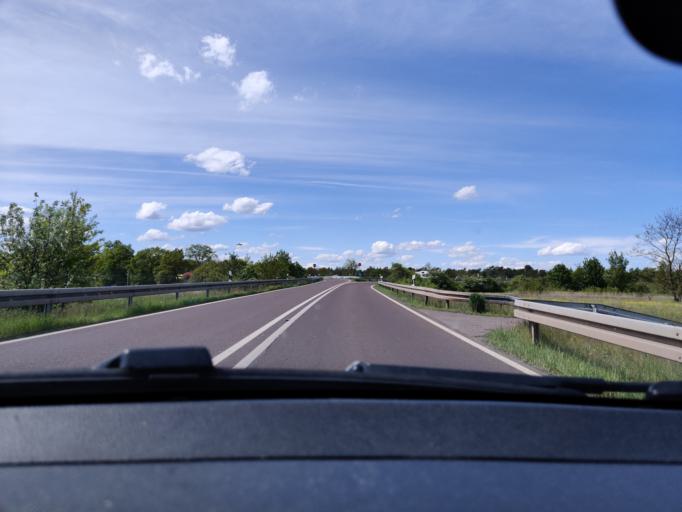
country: DE
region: Saxony-Anhalt
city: Burg bei Magdeburg
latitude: 52.2310
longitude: 11.8913
